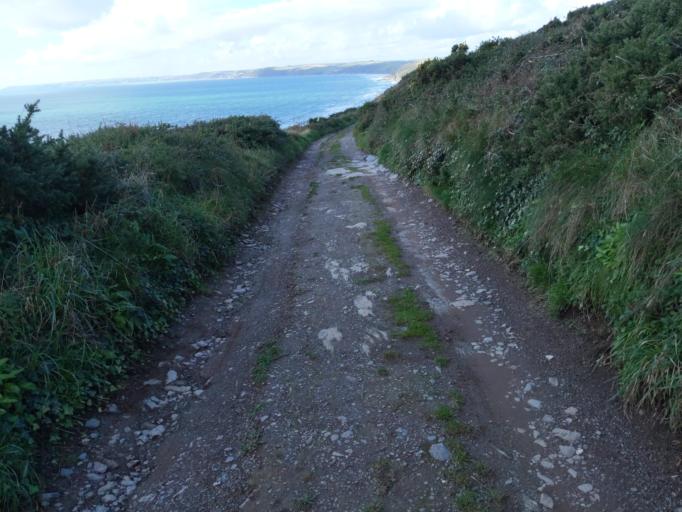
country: GB
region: England
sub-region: Cornwall
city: Torpoint
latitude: 50.3319
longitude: -4.2240
